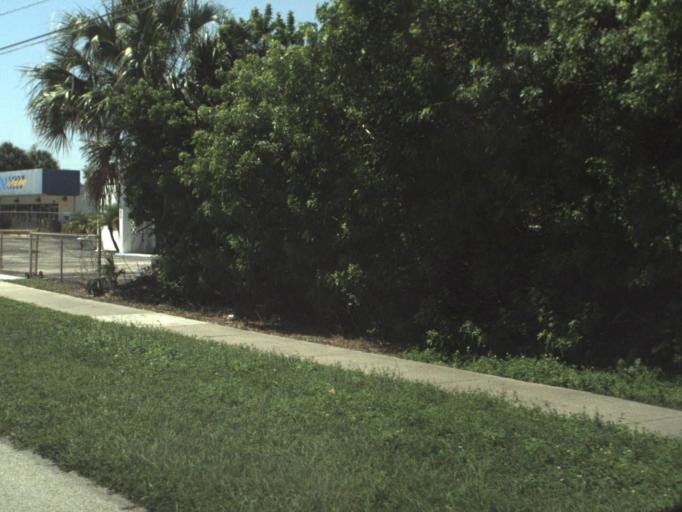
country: US
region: Florida
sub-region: Brevard County
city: Indialantic
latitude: 28.1096
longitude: -80.5728
